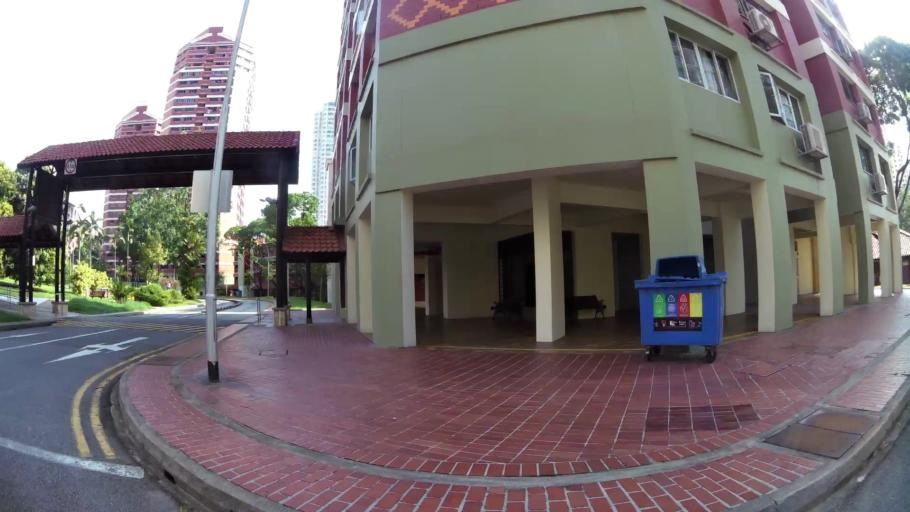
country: SG
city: Singapore
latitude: 1.3574
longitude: 103.8433
